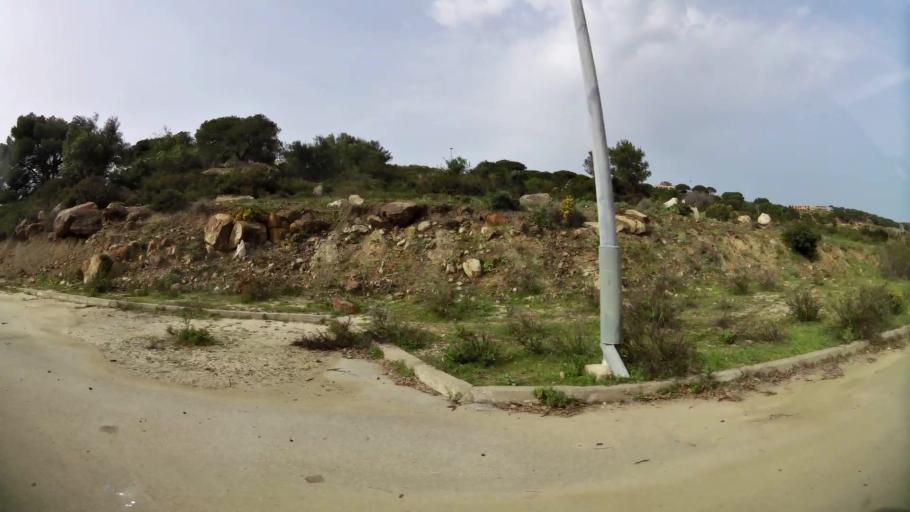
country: MA
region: Tanger-Tetouan
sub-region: Tanger-Assilah
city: Boukhalef
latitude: 35.6886
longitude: -5.9361
